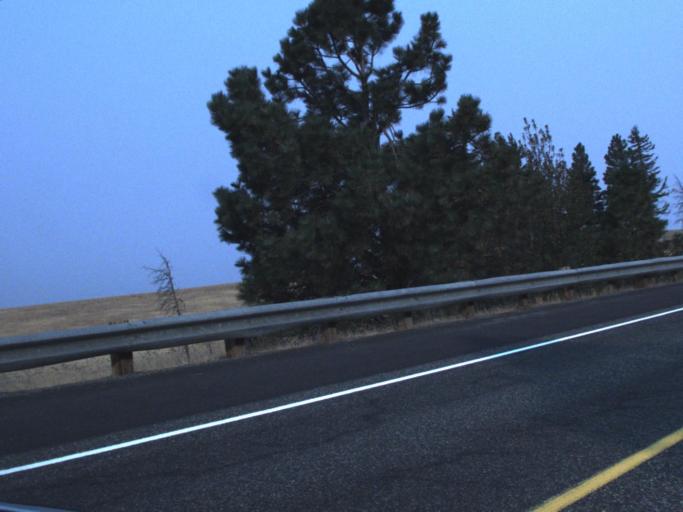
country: US
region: Washington
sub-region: Kittitas County
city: Ellensburg
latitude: 47.1583
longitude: -120.7024
